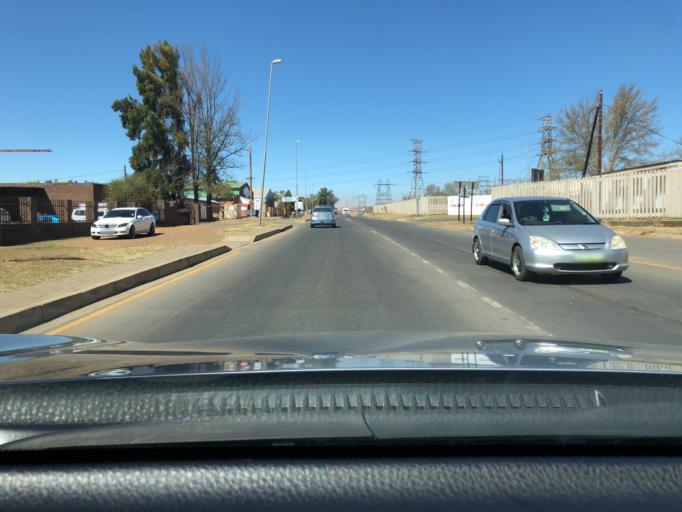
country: ZA
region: KwaZulu-Natal
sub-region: Amajuba District Municipality
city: Newcastle
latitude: -27.7606
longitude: 29.9526
